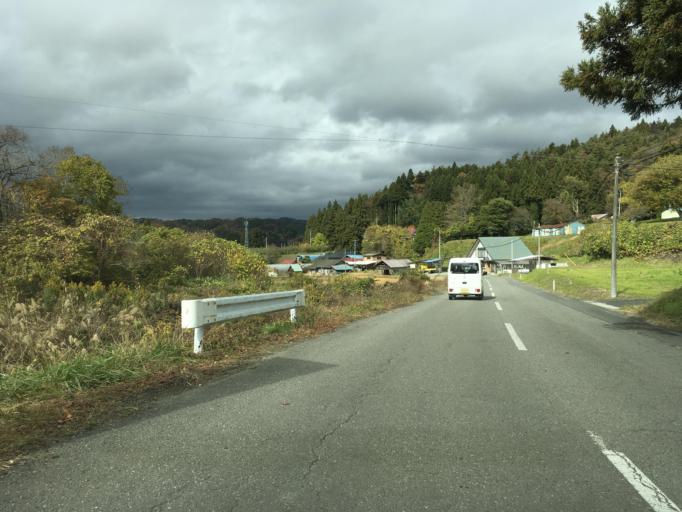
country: JP
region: Iwate
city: Mizusawa
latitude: 39.0629
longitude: 141.3874
